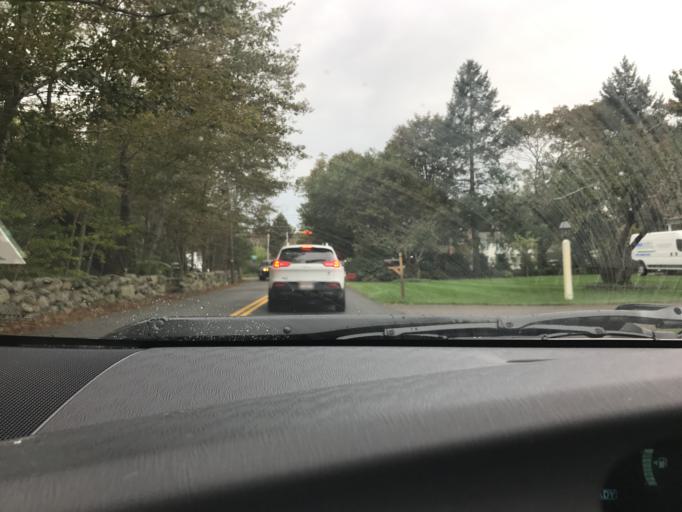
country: US
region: Massachusetts
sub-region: Middlesex County
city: Concord
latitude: 42.4742
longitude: -71.3637
